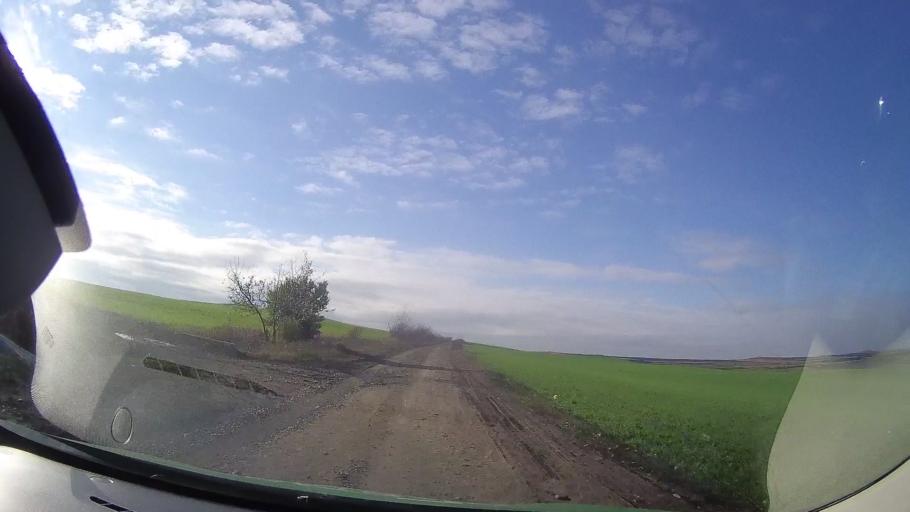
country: RO
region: Mures
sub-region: Comuna Saulia
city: Saulia
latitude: 46.6019
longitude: 24.2396
